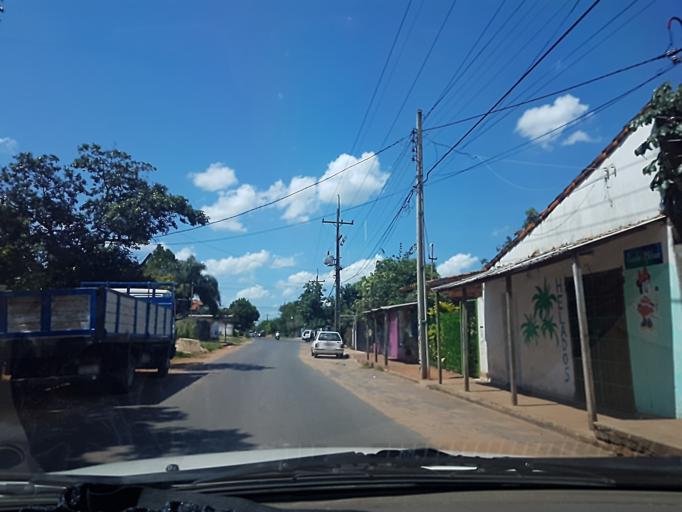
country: PY
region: Central
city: San Lorenzo
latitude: -25.2588
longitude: -57.4948
